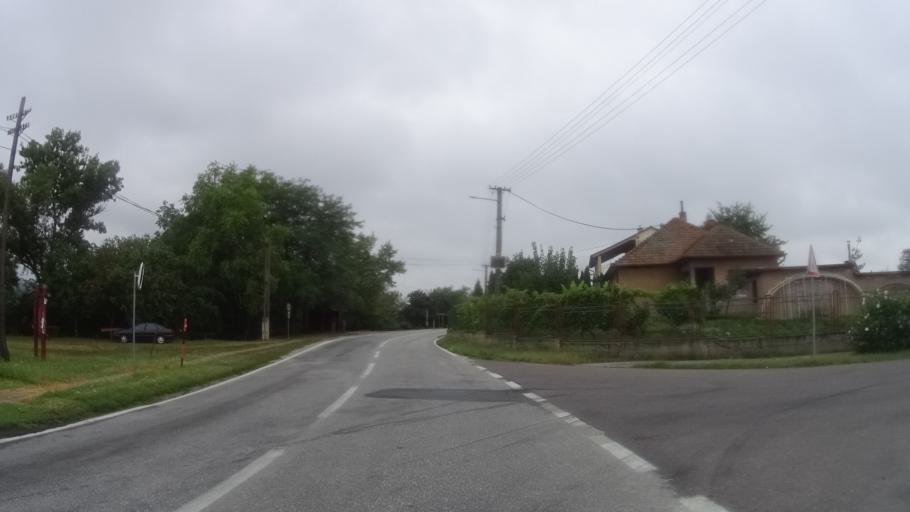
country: HU
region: Komarom-Esztergom
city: Neszmely
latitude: 47.7484
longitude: 18.3764
